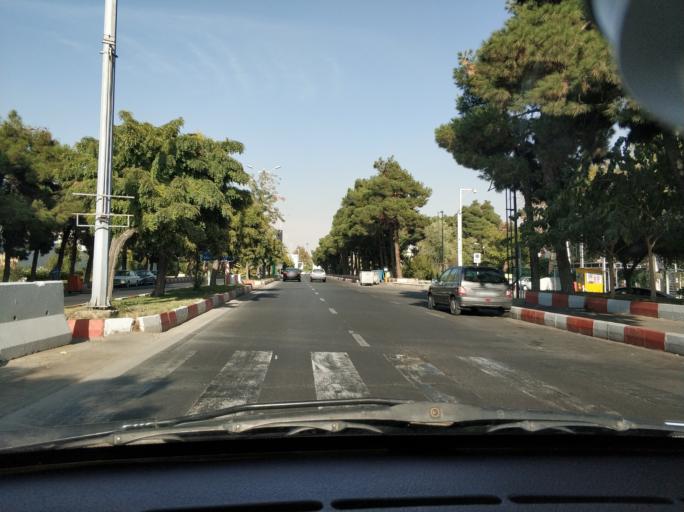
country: IR
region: Tehran
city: Tehran
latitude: 35.6974
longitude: 51.3320
